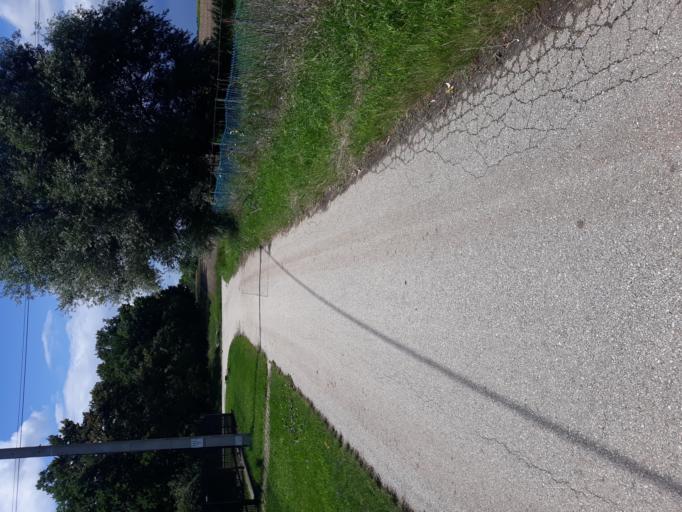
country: HU
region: Jasz-Nagykun-Szolnok
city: Kunmadaras
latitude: 47.3883
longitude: 20.8353
